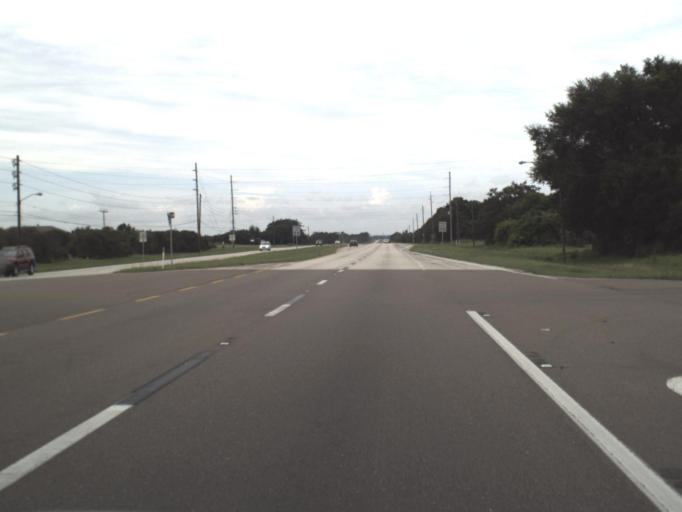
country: US
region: Florida
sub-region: Polk County
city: Eagle Lake
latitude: 27.9747
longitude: -81.7623
